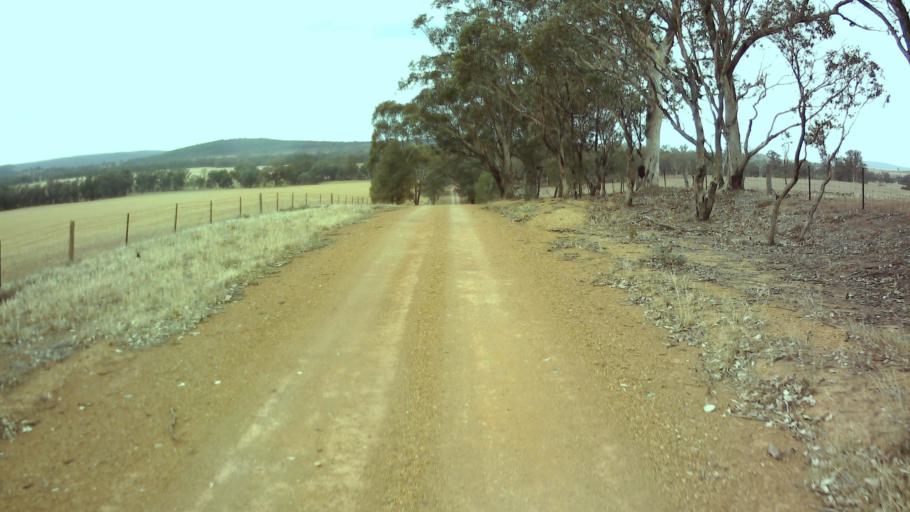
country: AU
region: New South Wales
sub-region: Weddin
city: Grenfell
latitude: -33.9277
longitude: 148.2544
